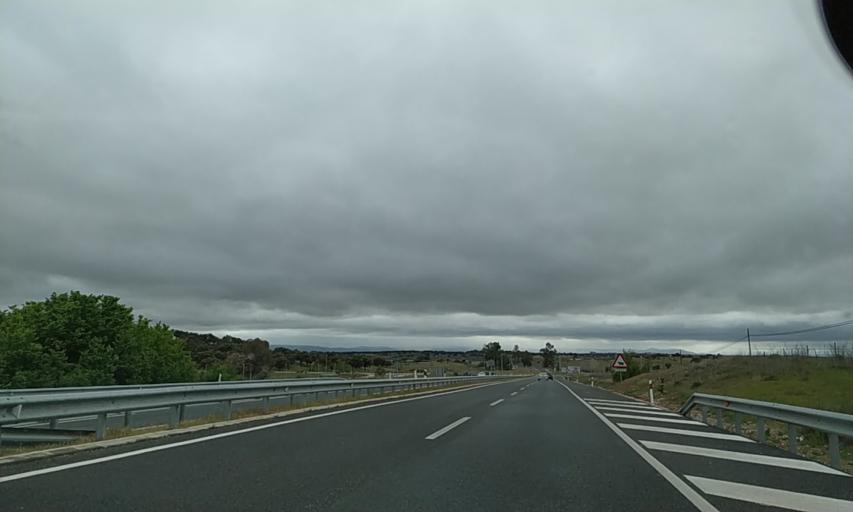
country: ES
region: Extremadura
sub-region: Provincia de Caceres
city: Caceres
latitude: 39.4667
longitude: -6.4028
